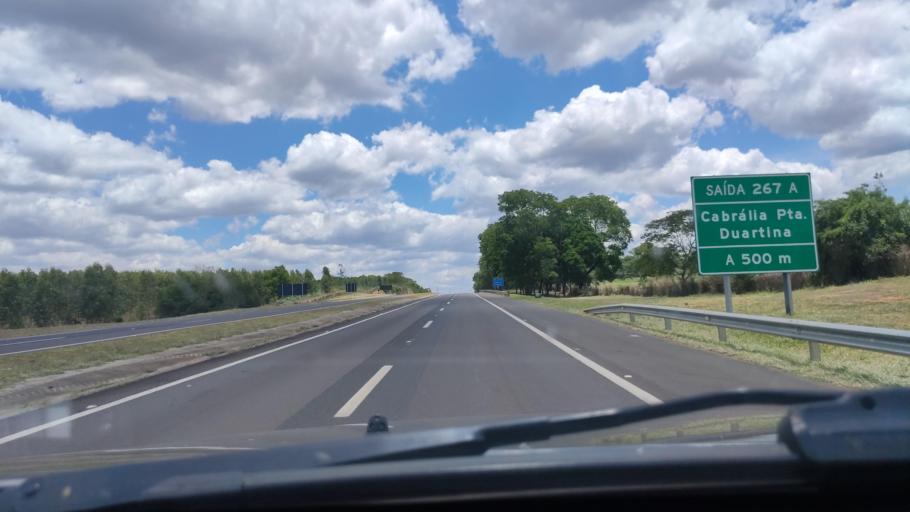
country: BR
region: Sao Paulo
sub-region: Duartina
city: Duartina
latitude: -22.5067
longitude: -49.2908
